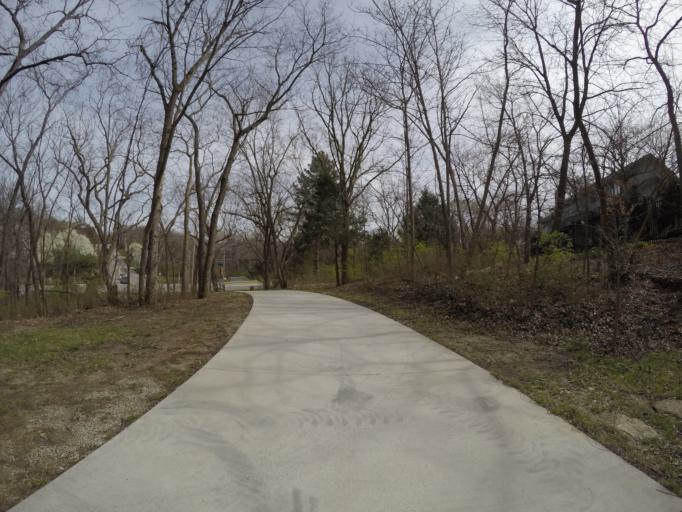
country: US
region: Kansas
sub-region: Johnson County
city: Leawood
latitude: 38.9058
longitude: -94.6313
